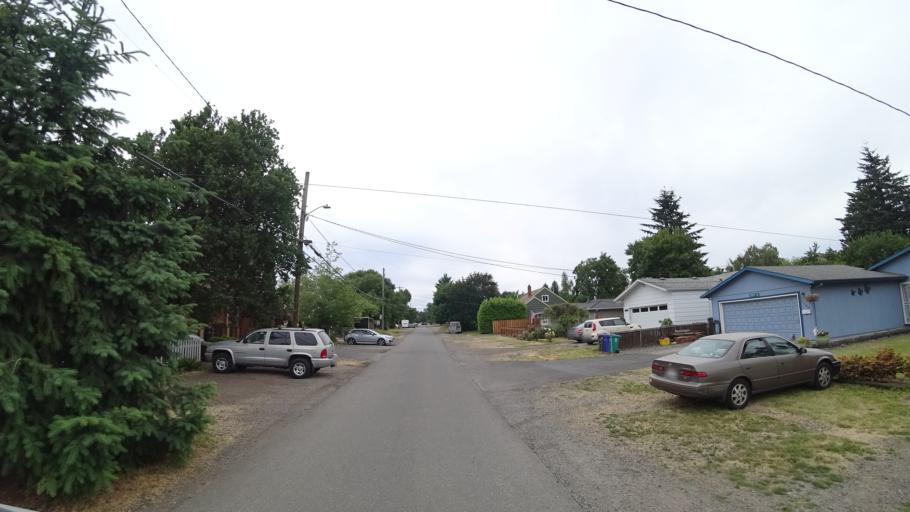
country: US
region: Oregon
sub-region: Multnomah County
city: Lents
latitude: 45.5146
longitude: -122.5752
